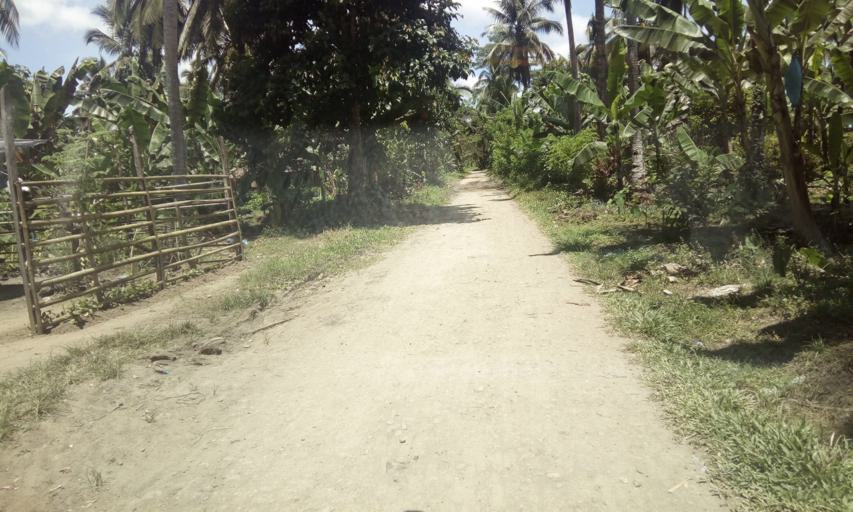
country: PH
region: Caraga
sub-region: Province of Agusan del Sur
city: Santa Josefa
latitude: 7.9523
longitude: 125.9984
